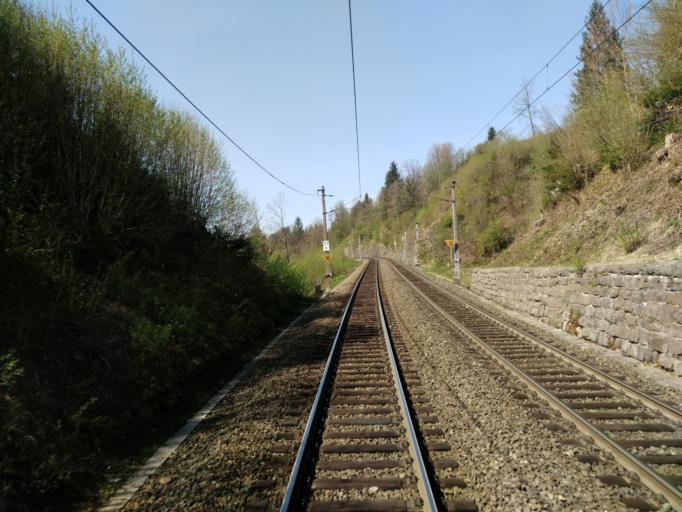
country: AT
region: Tyrol
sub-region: Politischer Bezirk Kitzbuhel
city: Hopfgarten im Brixental
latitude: 47.4303
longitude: 12.1836
